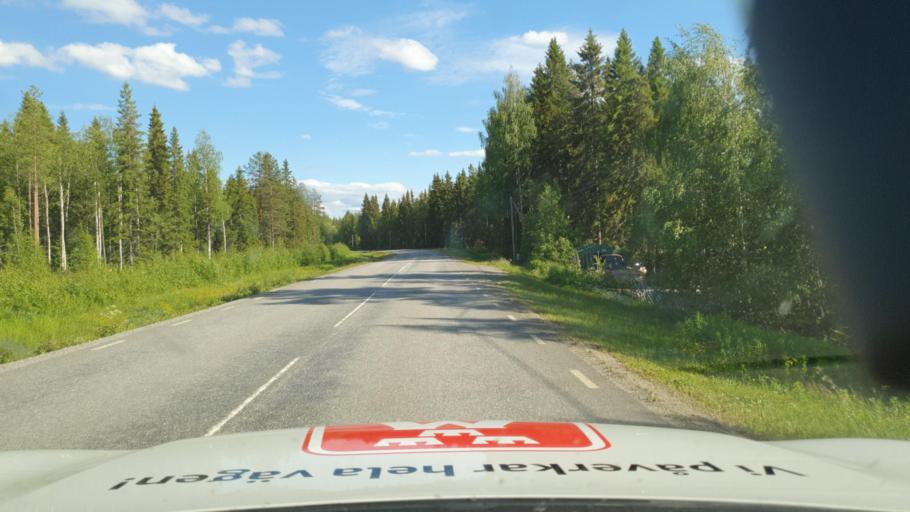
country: SE
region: Vaesterbotten
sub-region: Norsjo Kommun
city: Norsjoe
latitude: 64.8386
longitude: 19.7651
